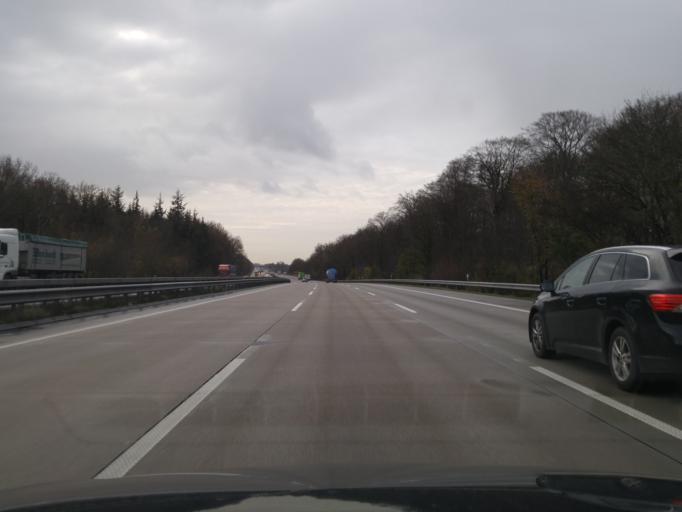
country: DE
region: Schleswig-Holstein
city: Lasbek
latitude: 53.7497
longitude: 10.3665
